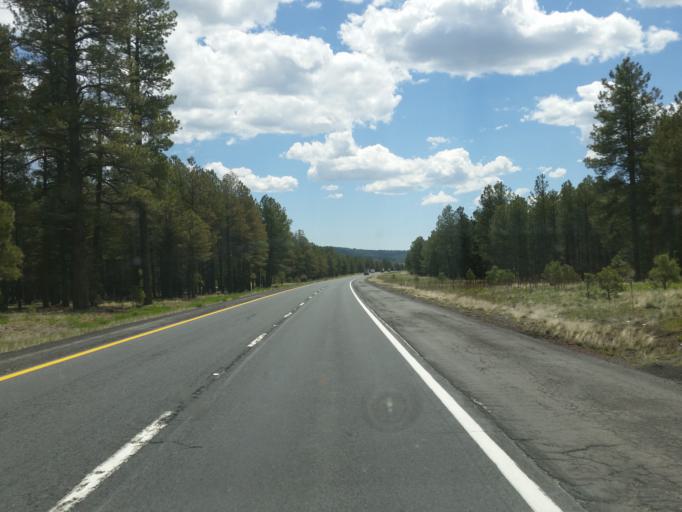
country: US
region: Arizona
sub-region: Coconino County
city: Parks
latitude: 35.2476
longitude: -111.8531
